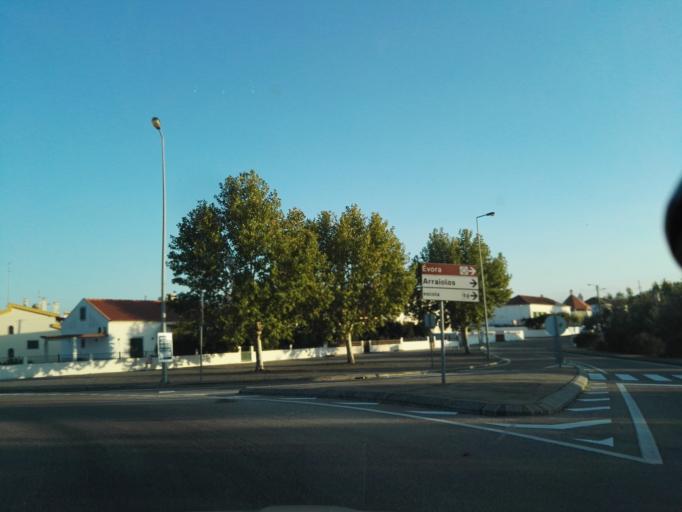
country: PT
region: Evora
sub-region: Mora
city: Mora
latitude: 38.8927
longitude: -8.0180
